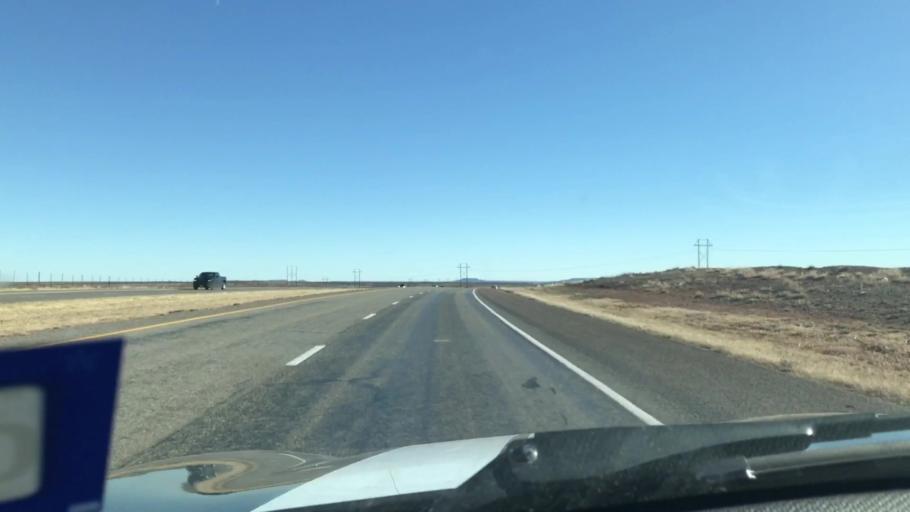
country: US
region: Texas
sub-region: Garza County
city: Post
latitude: 33.1191
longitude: -101.2801
